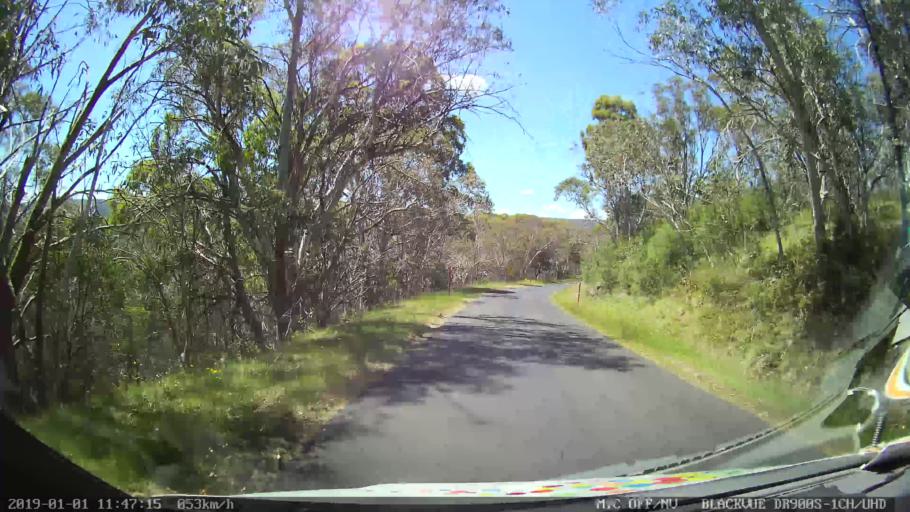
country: AU
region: New South Wales
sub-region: Snowy River
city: Jindabyne
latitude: -35.8902
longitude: 148.4030
